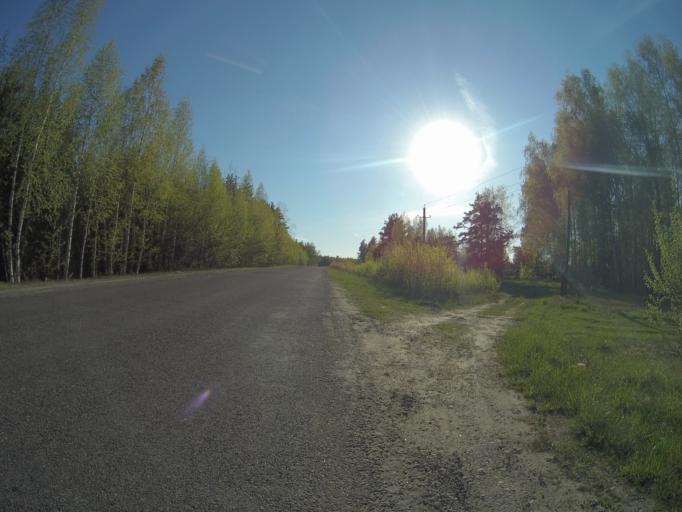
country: RU
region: Vladimir
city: Sudogda
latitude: 56.0605
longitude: 40.8186
